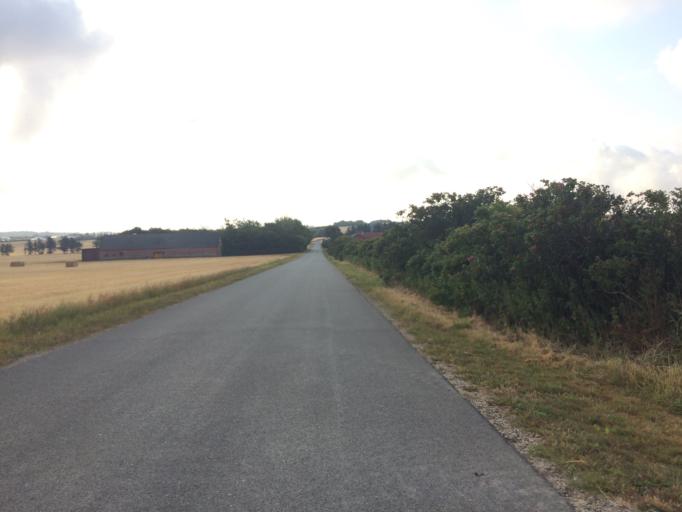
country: DK
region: Central Jutland
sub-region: Holstebro Kommune
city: Vinderup
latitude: 56.6048
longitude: 8.7074
